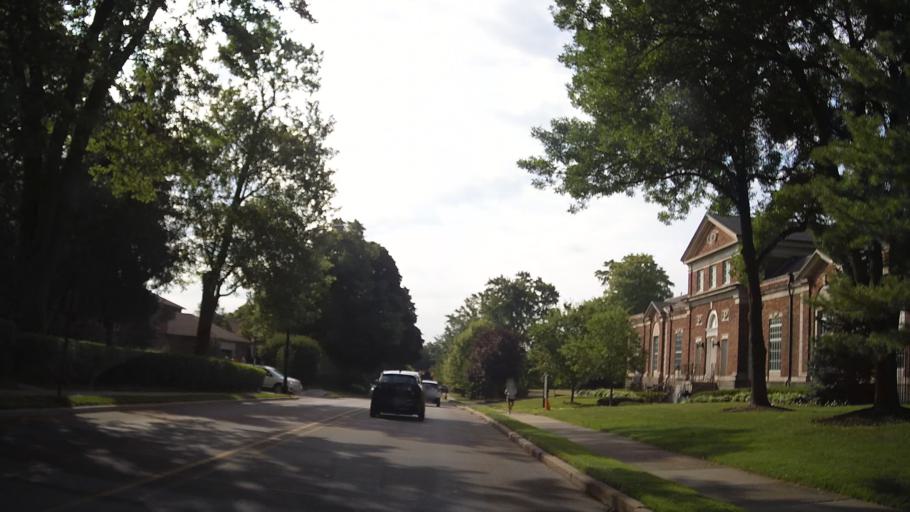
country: US
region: Michigan
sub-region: Wayne County
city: Grosse Pointe Farms
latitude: 42.4083
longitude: -82.8893
